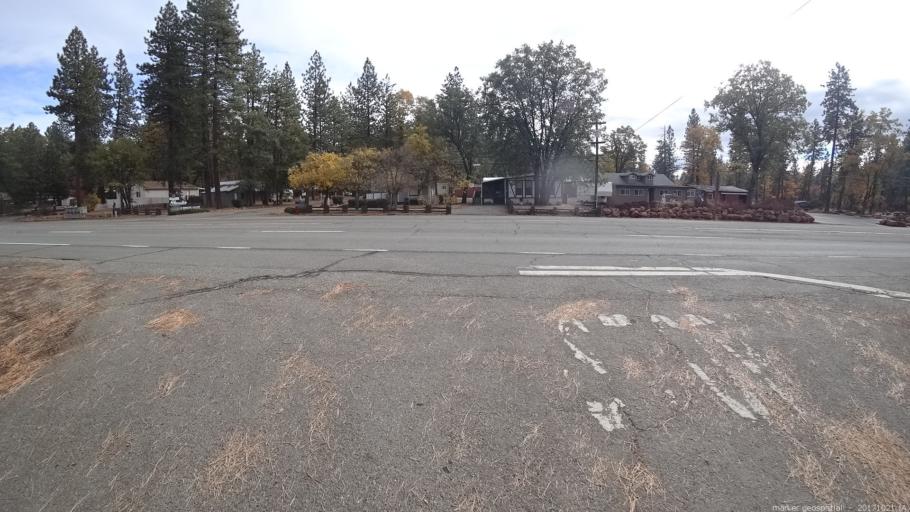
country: US
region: California
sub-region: Shasta County
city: Burney
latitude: 40.9218
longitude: -121.6235
